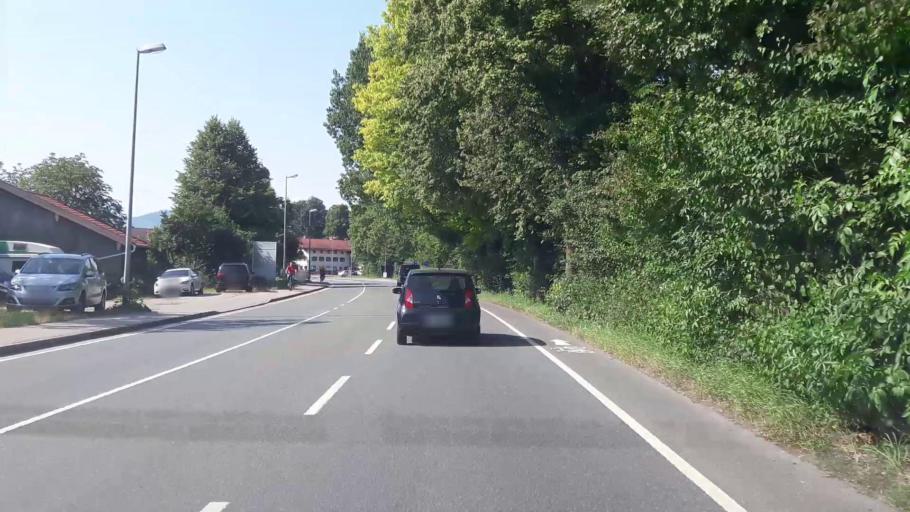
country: DE
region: Bavaria
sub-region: Upper Bavaria
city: Traunstein
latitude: 47.8638
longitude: 12.6285
